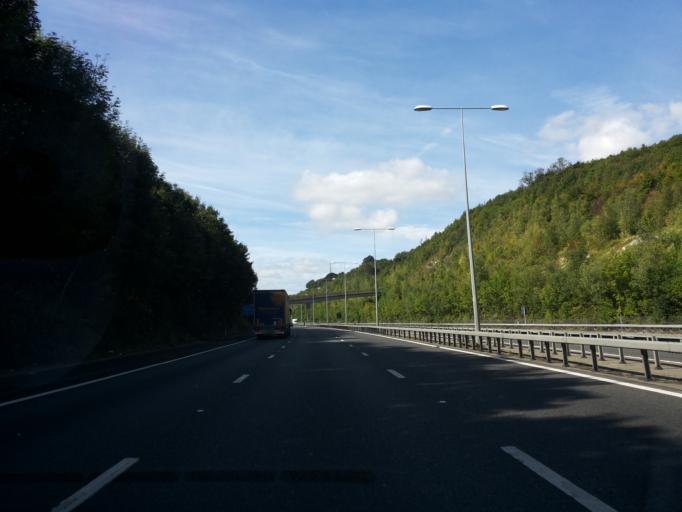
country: GB
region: England
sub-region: Kent
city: Borough Green
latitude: 51.3129
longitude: 0.3088
